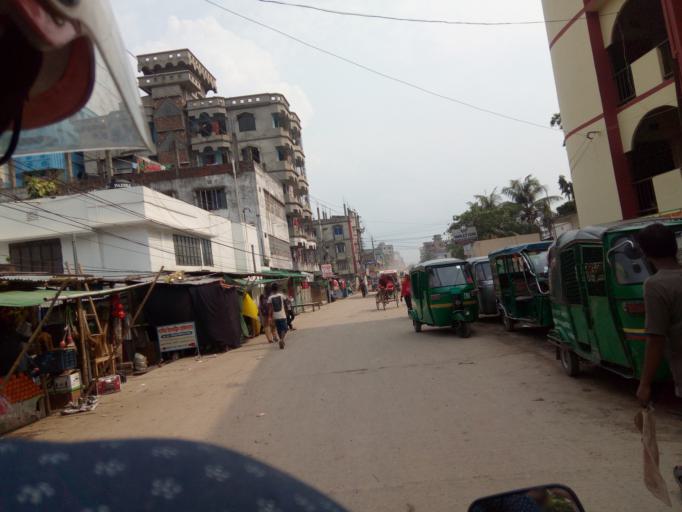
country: BD
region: Dhaka
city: Paltan
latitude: 23.7126
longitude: 90.4527
